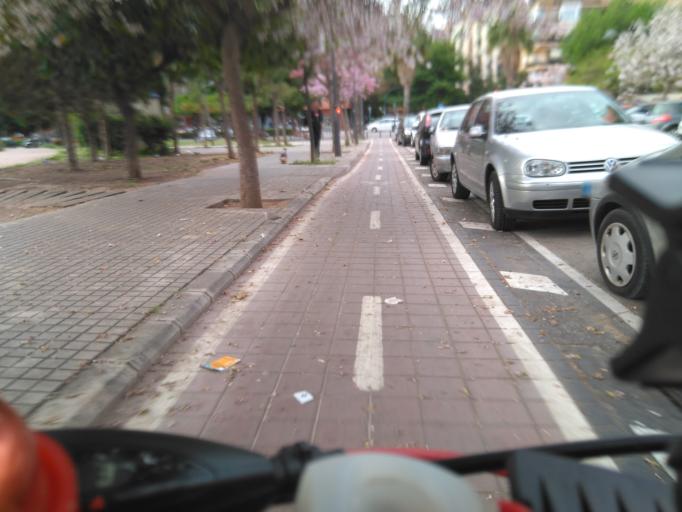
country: ES
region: Valencia
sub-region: Provincia de Valencia
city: Valencia
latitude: 39.4864
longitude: -0.3835
